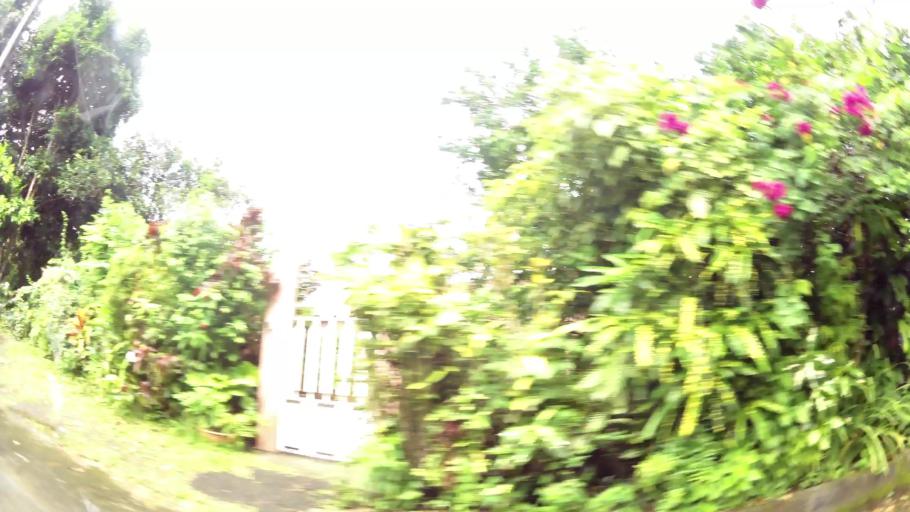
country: MQ
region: Martinique
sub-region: Martinique
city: Saint-Joseph
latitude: 14.6535
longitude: -61.0383
